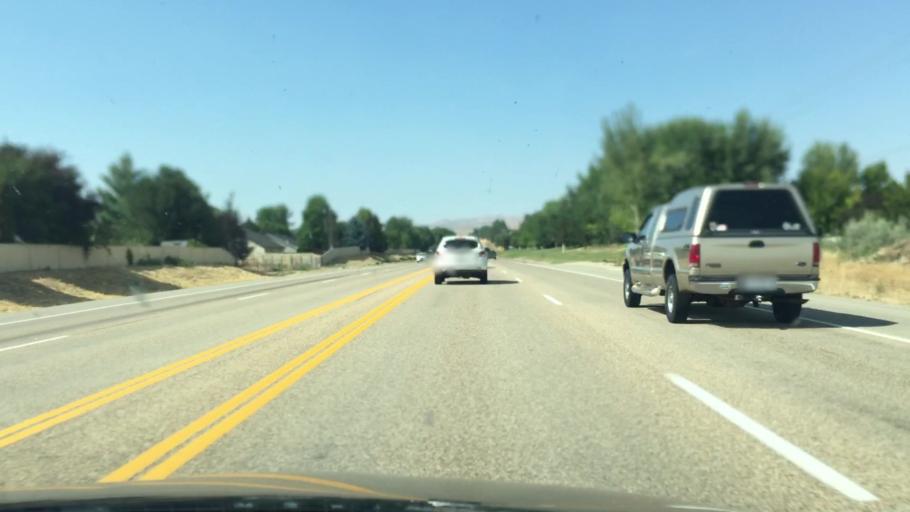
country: US
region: Idaho
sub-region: Ada County
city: Eagle
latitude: 43.7002
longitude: -116.3191
